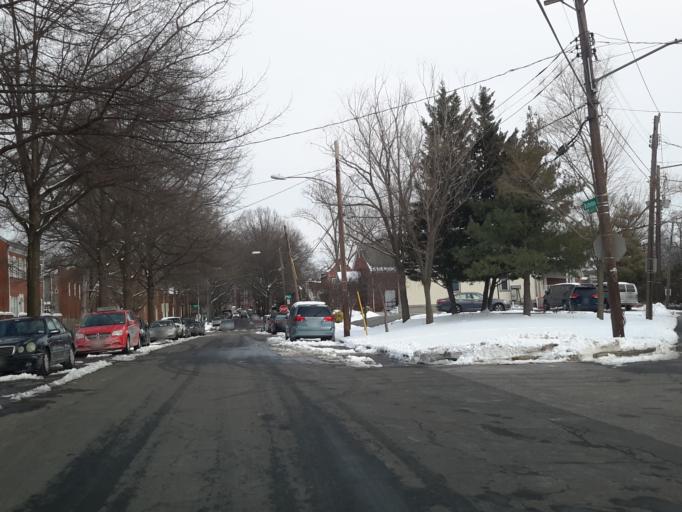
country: US
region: Maryland
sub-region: Montgomery County
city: Silver Spring
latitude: 38.9602
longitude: -77.0348
